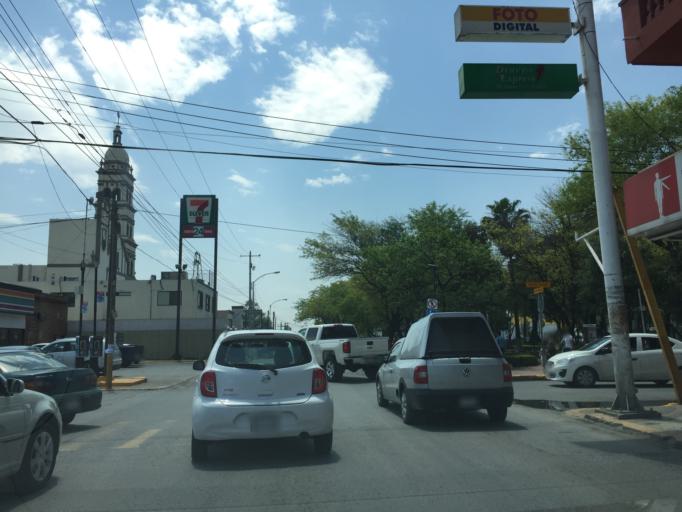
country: MX
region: Nuevo Leon
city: Apodaca
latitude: 25.7824
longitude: -100.1886
